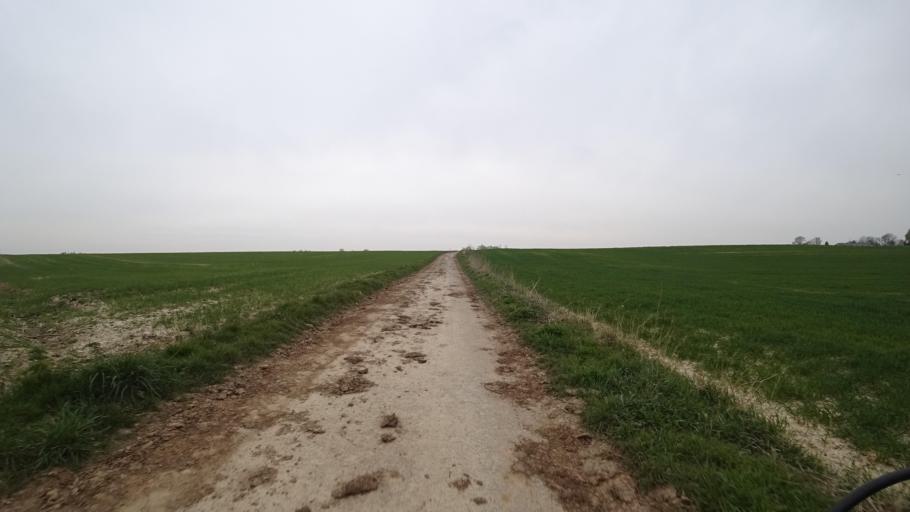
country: BE
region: Wallonia
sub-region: Province de Namur
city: Gembloux
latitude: 50.5903
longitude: 4.7081
